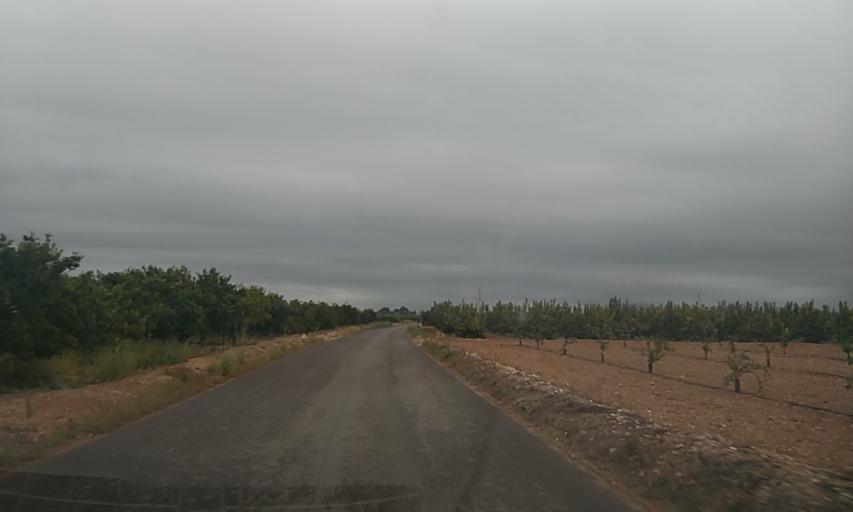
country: ES
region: Valencia
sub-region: Provincia de Valencia
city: Benimodo
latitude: 39.1887
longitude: -0.5328
